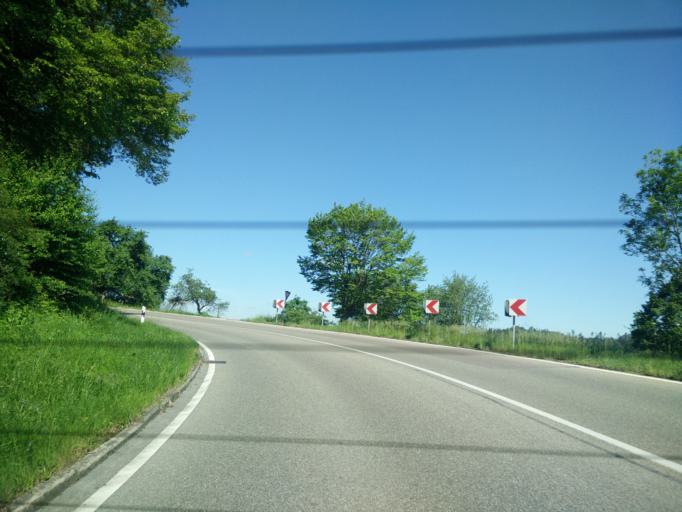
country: DE
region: Baden-Wuerttemberg
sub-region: Regierungsbezirk Stuttgart
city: Gaildorf
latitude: 48.9753
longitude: 9.7688
